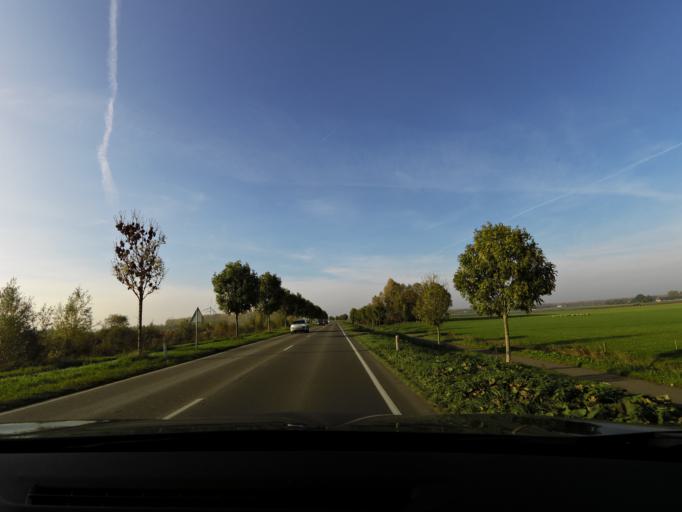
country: NL
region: North Brabant
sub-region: Gemeente Rucphen
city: Rucphen
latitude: 51.6115
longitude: 4.6502
